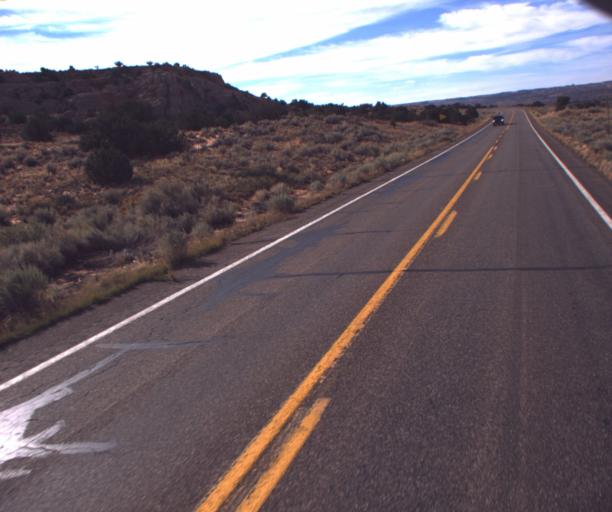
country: US
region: Arizona
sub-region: Coconino County
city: Kaibito
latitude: 36.6770
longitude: -111.2558
